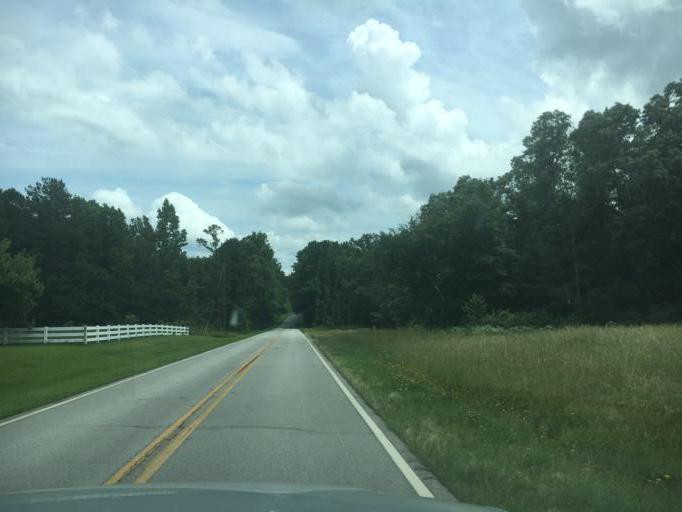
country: US
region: Georgia
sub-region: Hart County
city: Reed Creek
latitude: 34.4370
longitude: -82.9556
